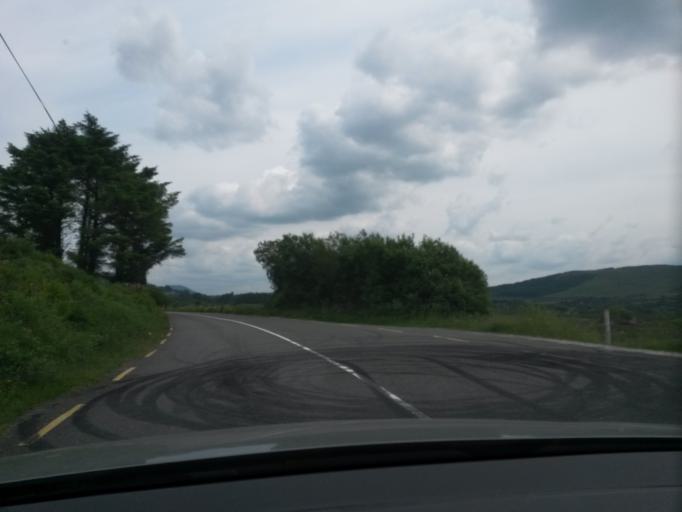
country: IE
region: Munster
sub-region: Ciarrai
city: Kenmare
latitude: 51.9084
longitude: -9.7253
